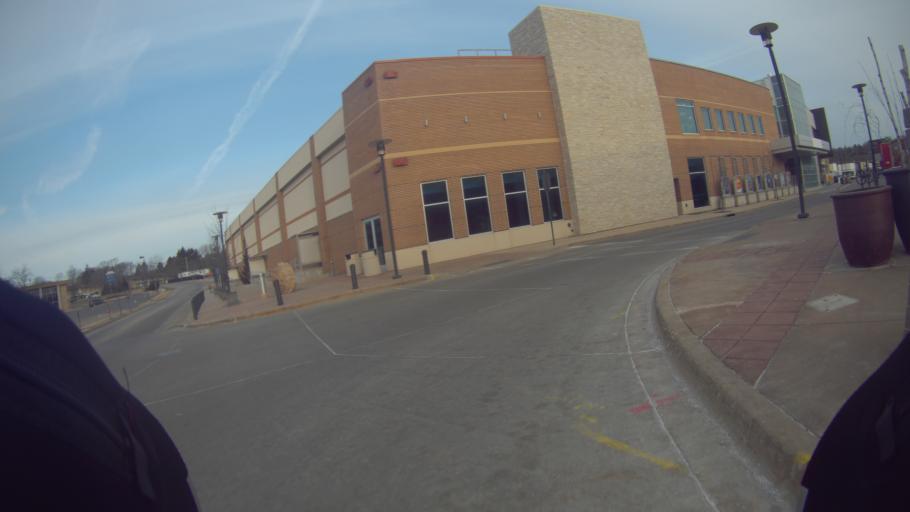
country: US
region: Wisconsin
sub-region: Dane County
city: Shorewood Hills
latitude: 43.0715
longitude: -89.4523
